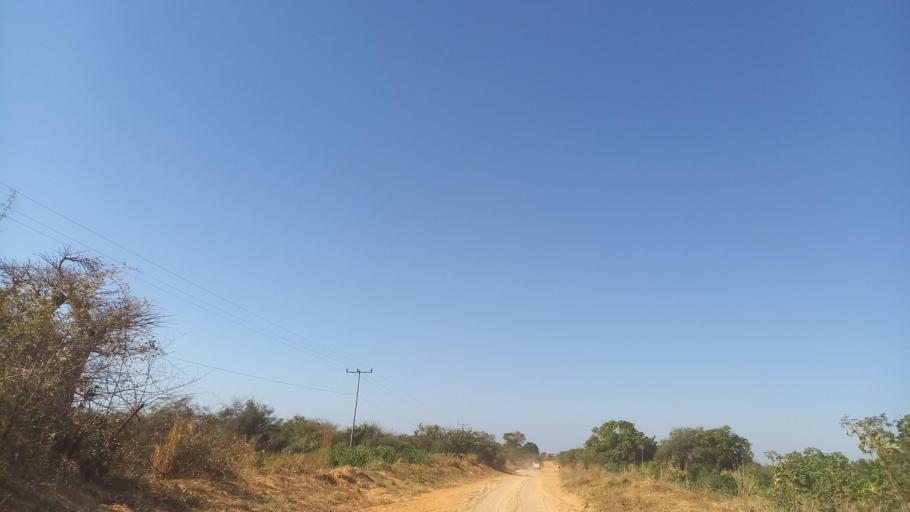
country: MZ
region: Cabo Delgado
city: Pemba
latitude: -13.1546
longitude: 40.5579
